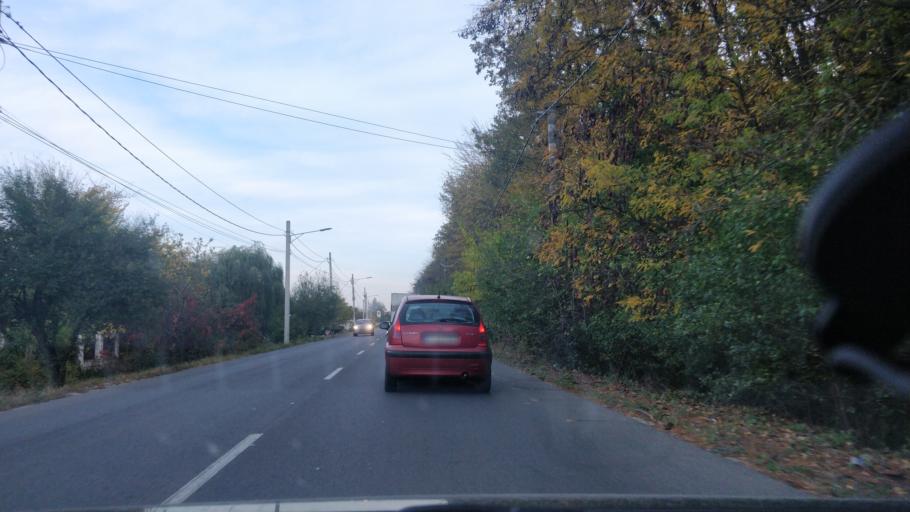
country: RO
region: Ilfov
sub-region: Comuna Ciorogarla
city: Ciorogarla
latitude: 44.4459
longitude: 25.8587
